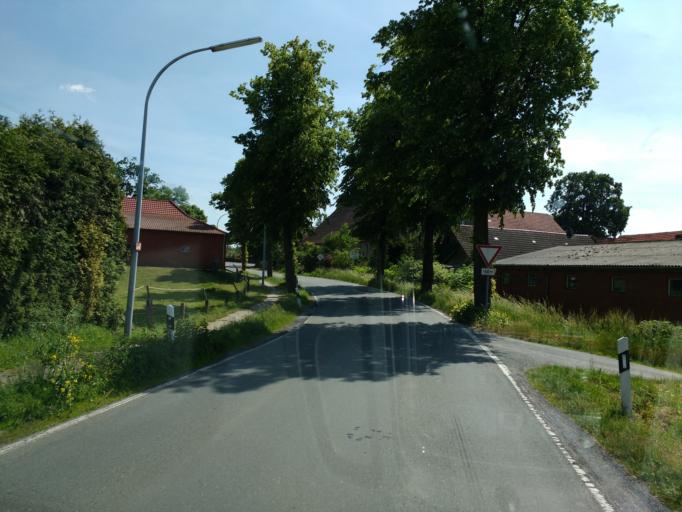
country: DE
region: Lower Saxony
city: Belm
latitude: 52.3399
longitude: 8.1104
